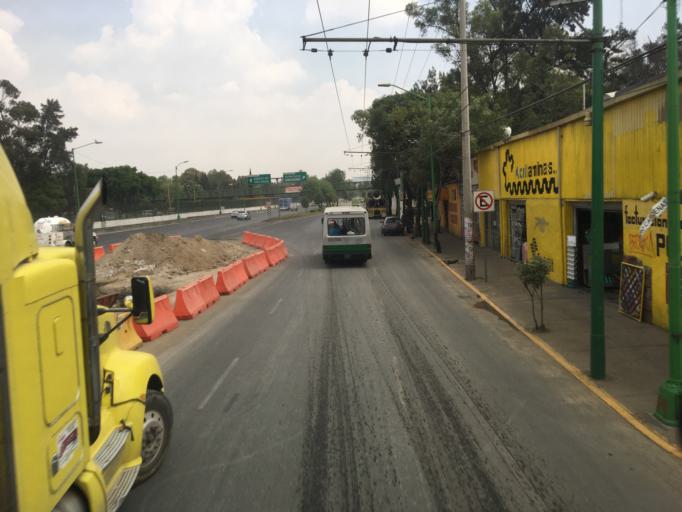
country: MX
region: Mexico
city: Colonia Lindavista
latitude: 19.4950
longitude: -99.1464
